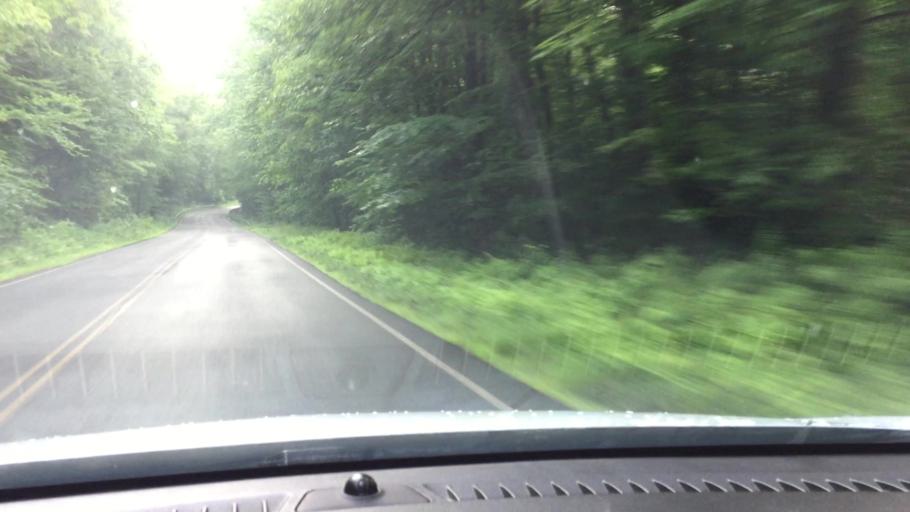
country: US
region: Massachusetts
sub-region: Hampshire County
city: Westhampton
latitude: 42.2538
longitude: -72.9058
